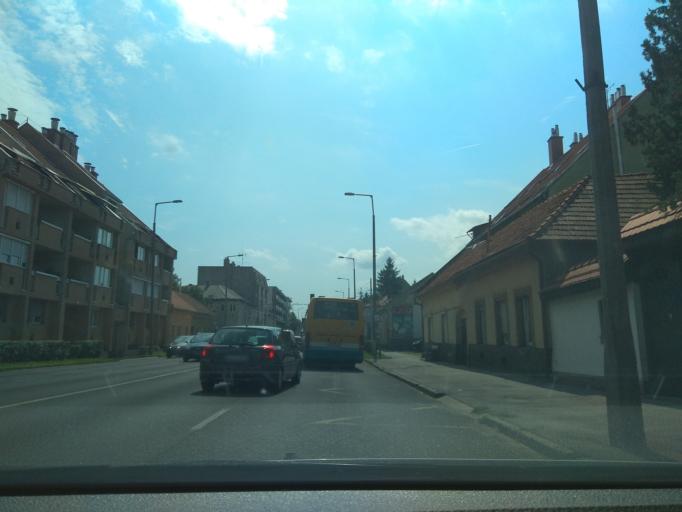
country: HU
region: Heves
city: Eger
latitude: 47.9042
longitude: 20.3665
